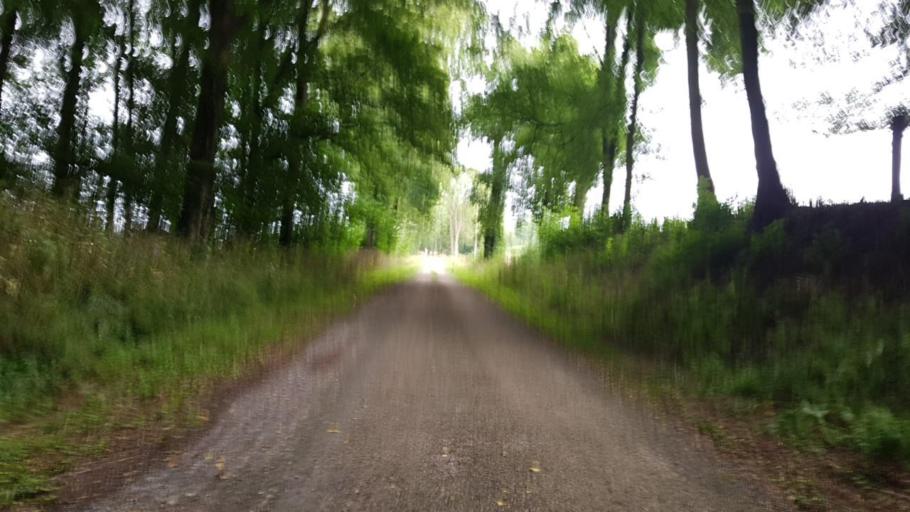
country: FR
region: Picardie
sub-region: Departement de l'Aisne
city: Guise
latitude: 49.8940
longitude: 3.7017
